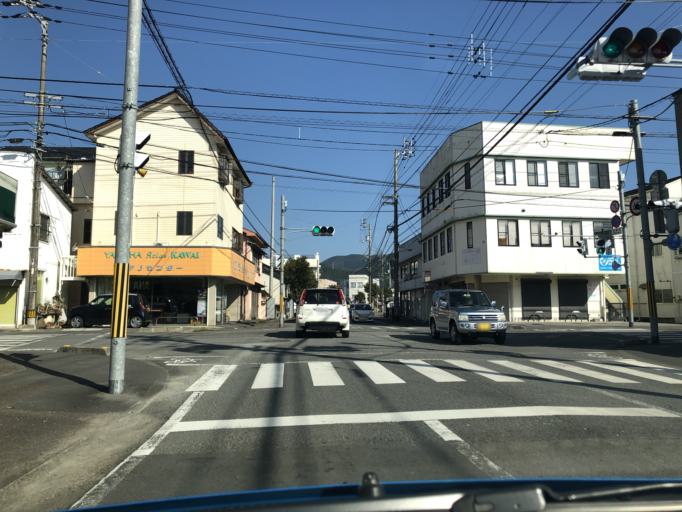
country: JP
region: Kochi
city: Sukumo
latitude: 32.9372
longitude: 132.7231
